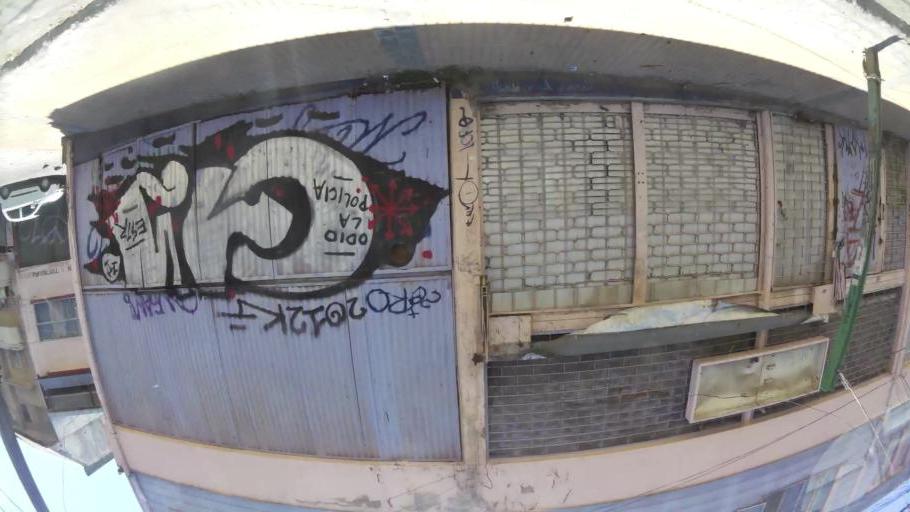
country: CL
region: Valparaiso
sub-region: Provincia de Valparaiso
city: Valparaiso
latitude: -33.0371
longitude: -71.6321
